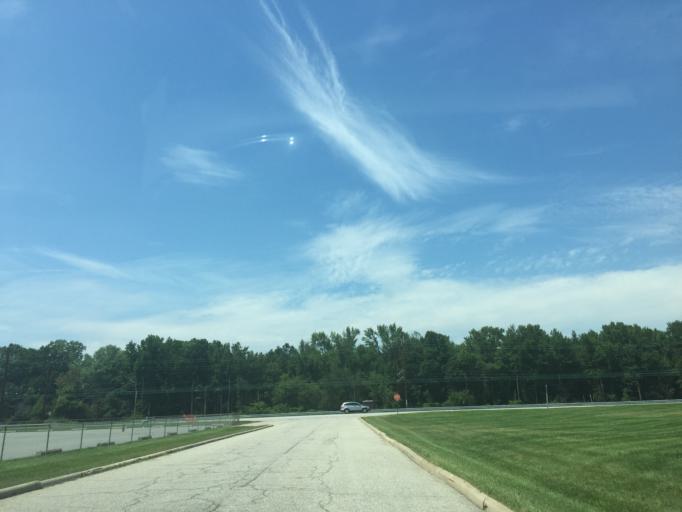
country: US
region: Maryland
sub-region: Baltimore County
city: Middle River
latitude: 39.3337
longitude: -76.4307
